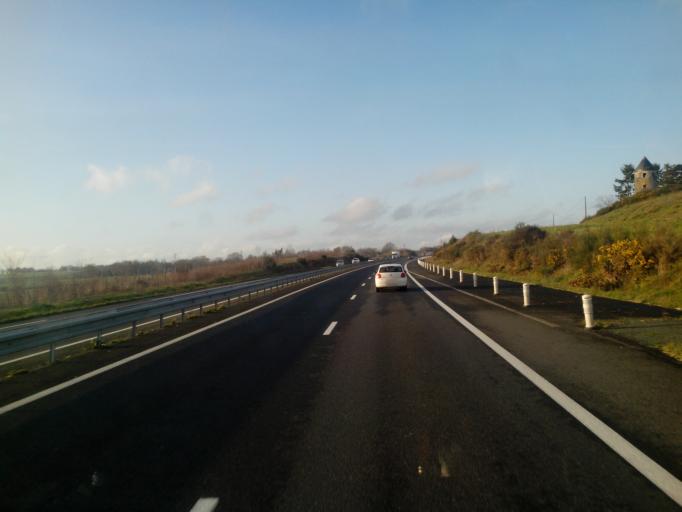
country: FR
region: Poitou-Charentes
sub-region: Departement des Deux-Sevres
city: Saint-Pierre-des-Echaubrognes
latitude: 46.9661
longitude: -0.7972
